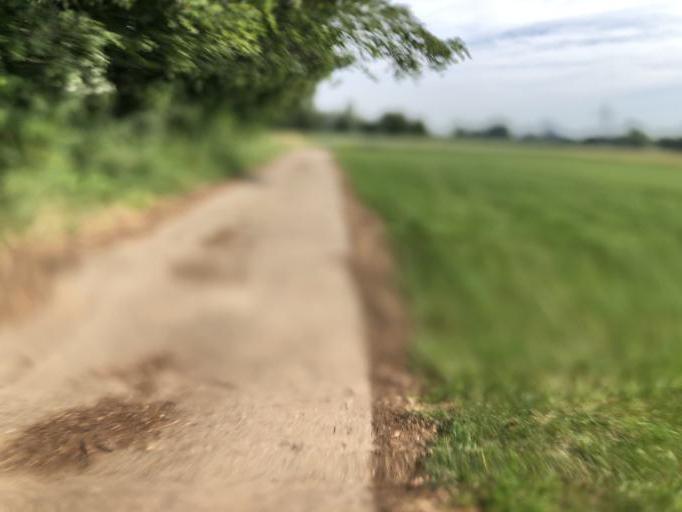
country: DE
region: Bavaria
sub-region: Regierungsbezirk Mittelfranken
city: Erlangen
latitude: 49.5607
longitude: 10.9786
